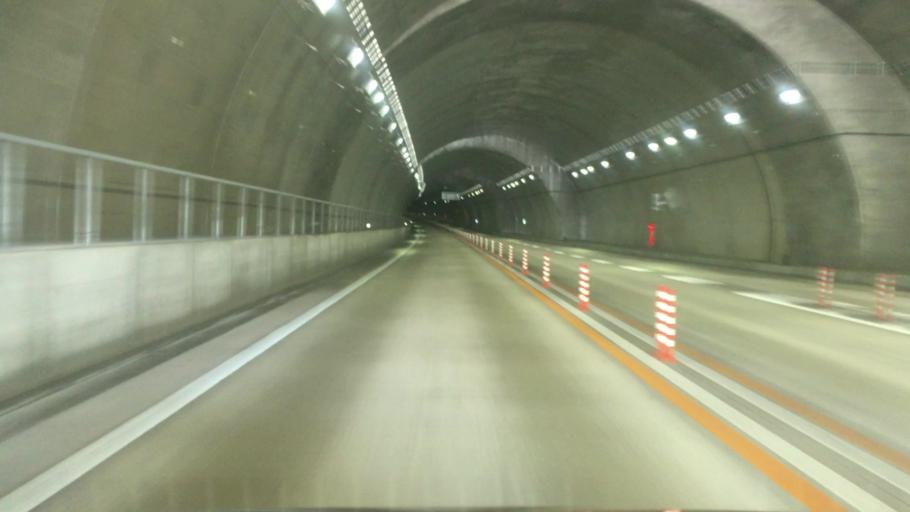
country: JP
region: Hyogo
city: Toyooka
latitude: 35.6398
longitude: 134.5623
